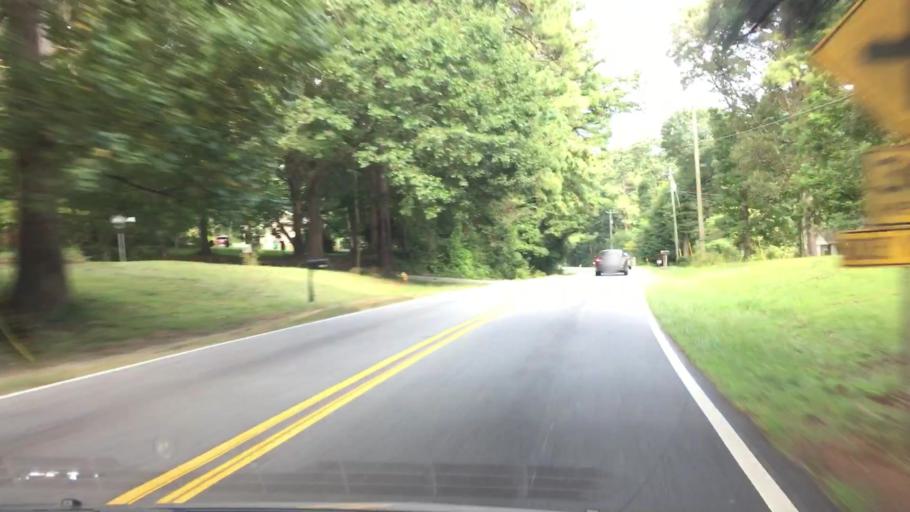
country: US
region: Georgia
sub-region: Clayton County
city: Conley
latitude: 33.6603
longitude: -84.2972
